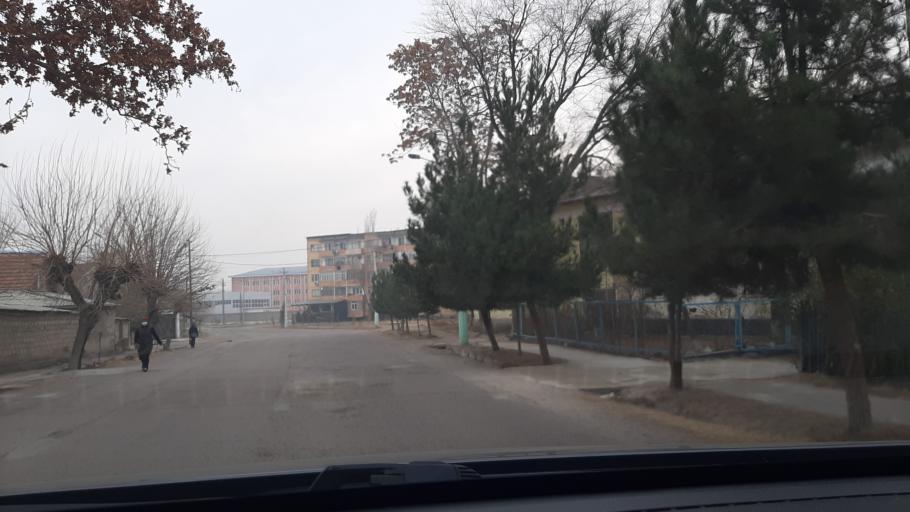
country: TJ
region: Viloyati Sughd
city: Palos
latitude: 40.2623
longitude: 69.7913
